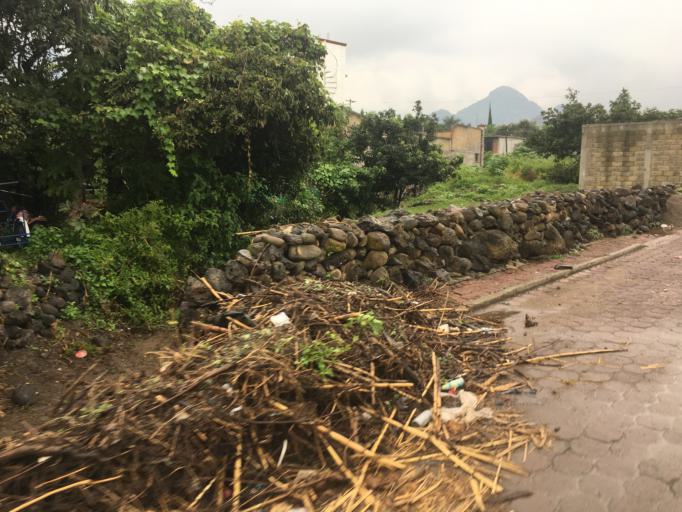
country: MX
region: Morelos
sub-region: Tlayacapan
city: Tlayacapan
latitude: 18.9579
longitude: -98.9864
